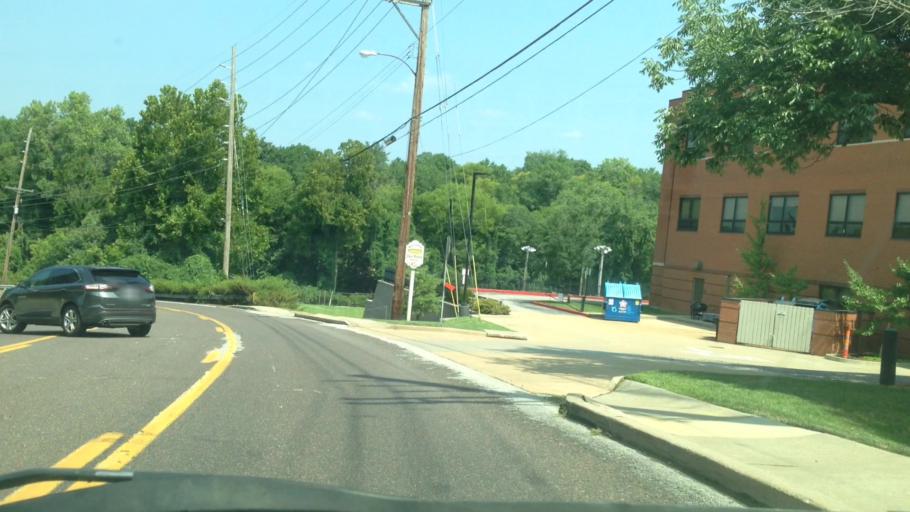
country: US
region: Missouri
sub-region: Saint Louis County
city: Des Peres
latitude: 38.5851
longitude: -90.4436
